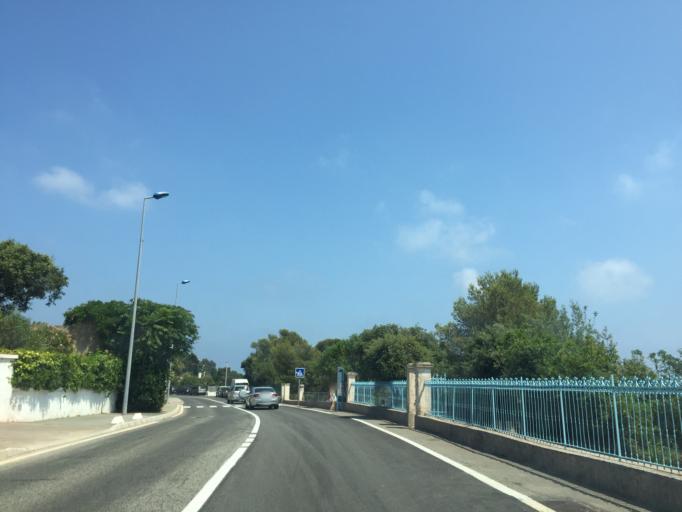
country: FR
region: Provence-Alpes-Cote d'Azur
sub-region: Departement des Alpes-Maritimes
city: Theoule-sur-Mer
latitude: 43.4283
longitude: 6.8797
